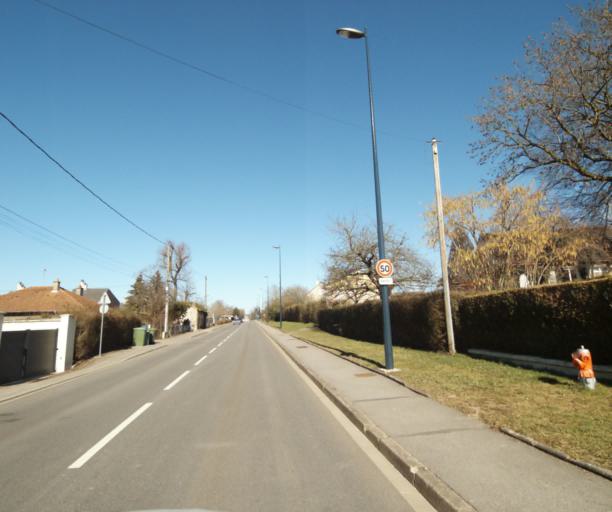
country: FR
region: Lorraine
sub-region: Departement de Meurthe-et-Moselle
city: Heillecourt
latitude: 48.6613
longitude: 6.2071
